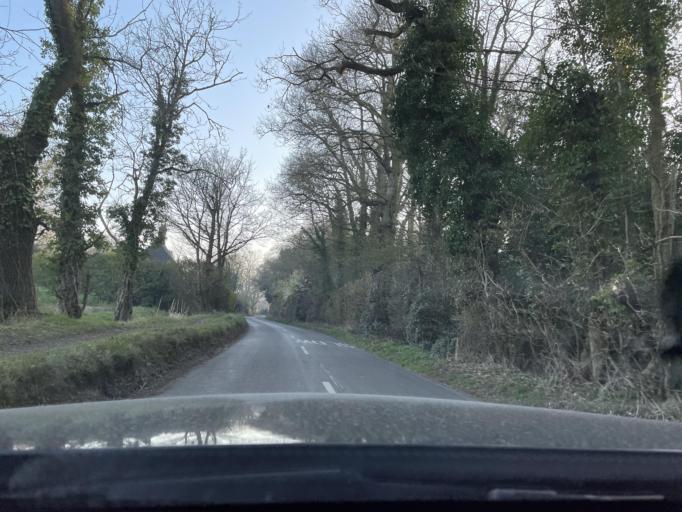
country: GB
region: England
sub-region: Norfolk
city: Martham
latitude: 52.7469
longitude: 1.6399
